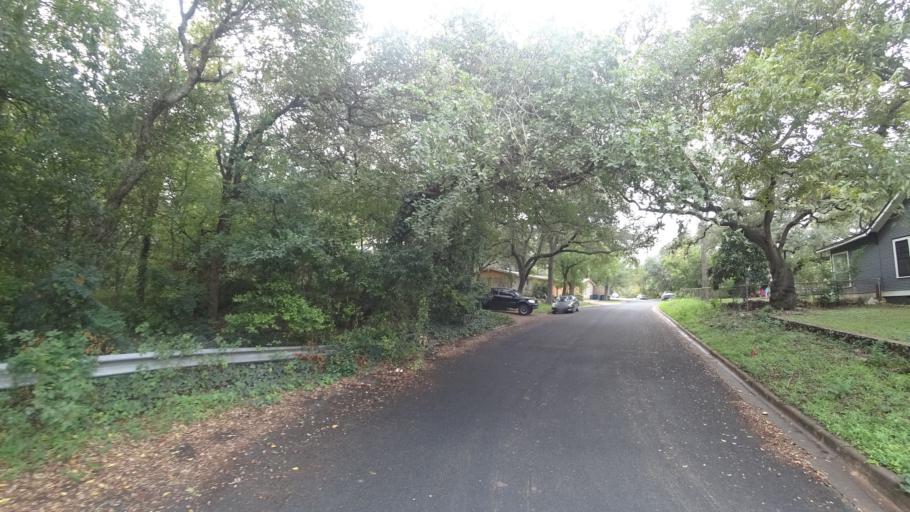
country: US
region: Texas
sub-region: Travis County
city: Austin
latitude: 30.2629
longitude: -97.7642
